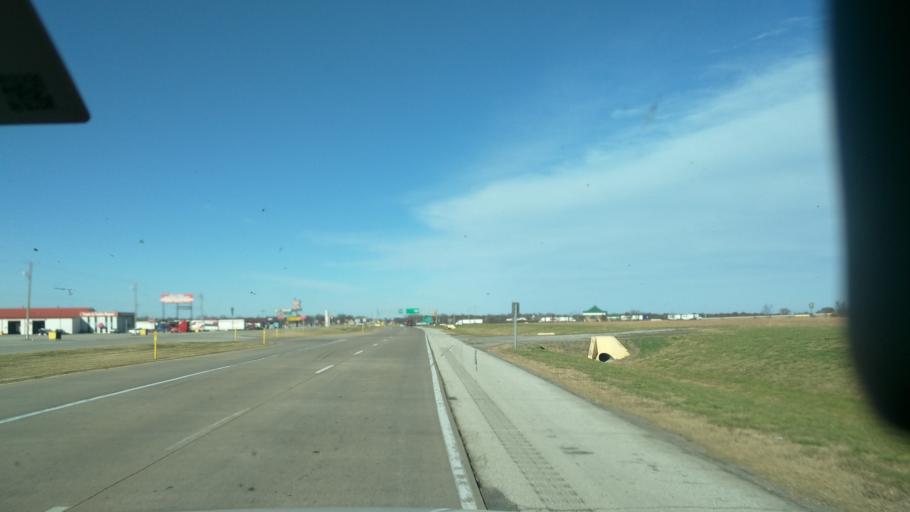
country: US
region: Oklahoma
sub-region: Craig County
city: Vinita
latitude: 36.5620
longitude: -95.2201
